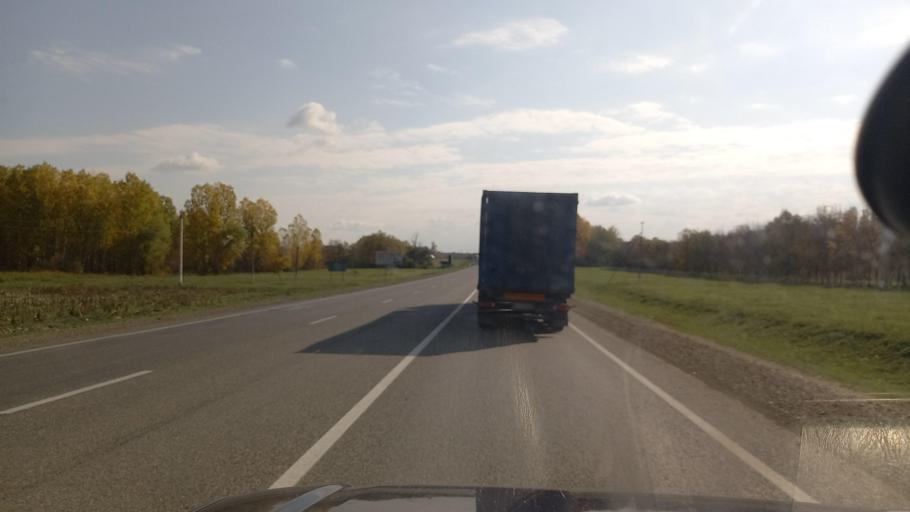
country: RU
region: Krasnodarskiy
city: Novoukrainskiy
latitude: 44.8866
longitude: 38.0825
